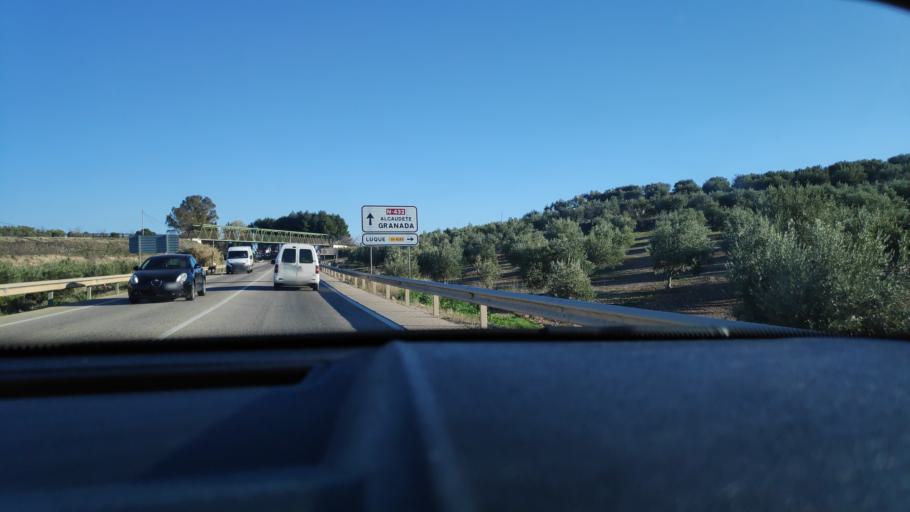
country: ES
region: Andalusia
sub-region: Province of Cordoba
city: Luque
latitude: 37.5746
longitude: -4.2674
